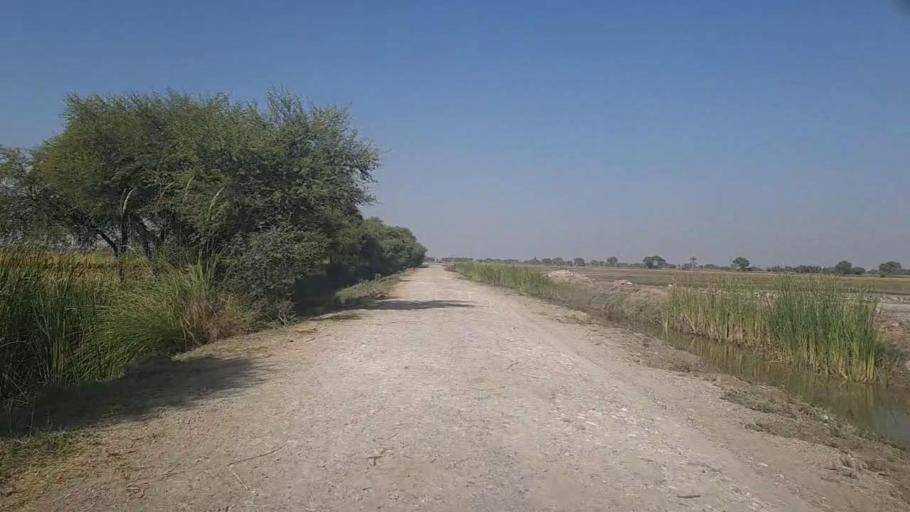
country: PK
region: Sindh
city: Thul
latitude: 28.3040
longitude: 68.7710
